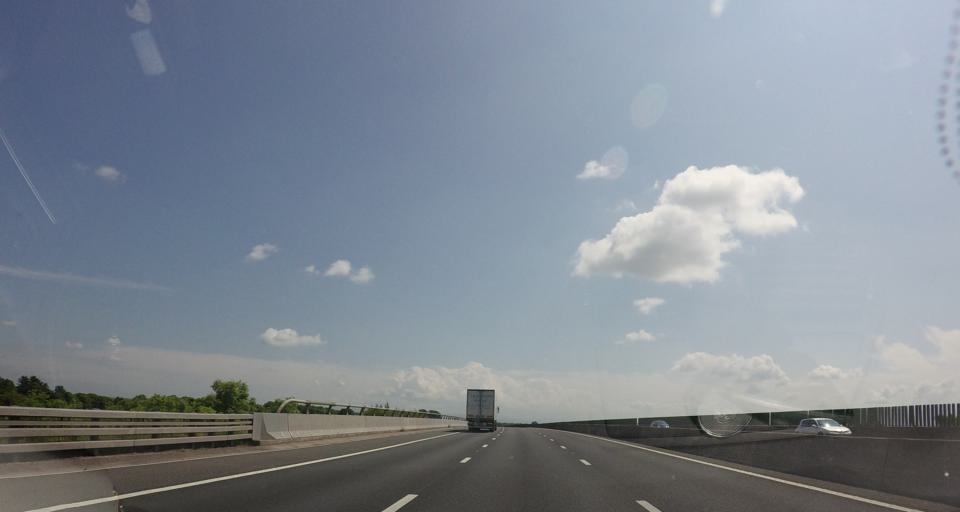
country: GB
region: Scotland
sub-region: Dumfries and Galloway
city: Gretna
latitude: 54.9811
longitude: -3.0258
